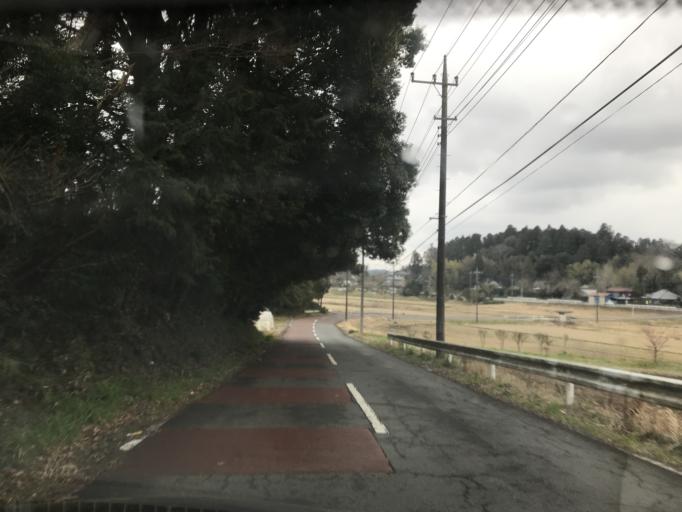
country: JP
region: Chiba
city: Sawara
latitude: 35.8226
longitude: 140.5063
